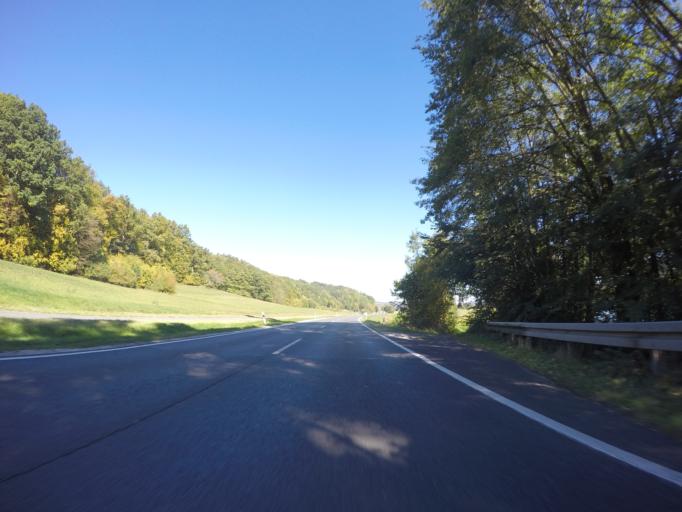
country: DE
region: Bavaria
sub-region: Upper Franconia
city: Wiesenthau
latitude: 49.7299
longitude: 11.1263
